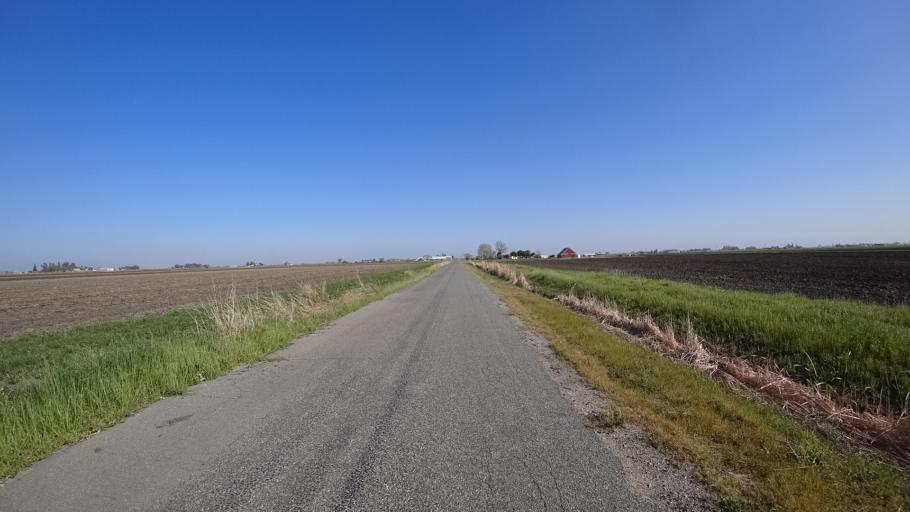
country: US
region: California
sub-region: Glenn County
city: Willows
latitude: 39.5659
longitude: -122.0839
